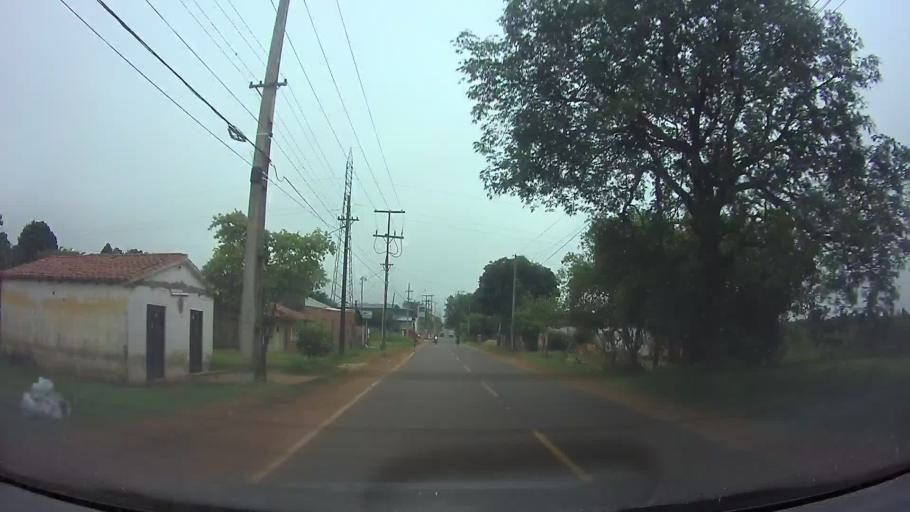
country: PY
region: Central
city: Itaugua
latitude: -25.3826
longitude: -57.3503
